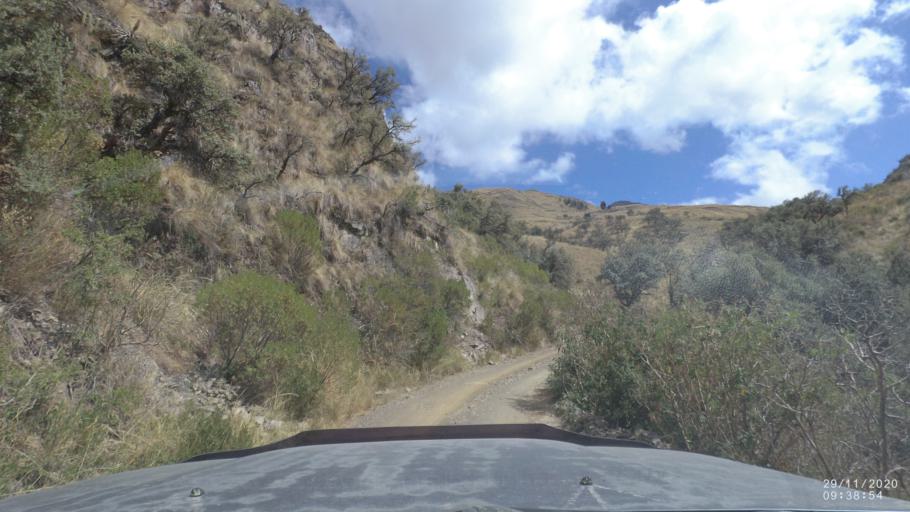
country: BO
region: Cochabamba
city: Cochabamba
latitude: -17.3056
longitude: -66.1847
